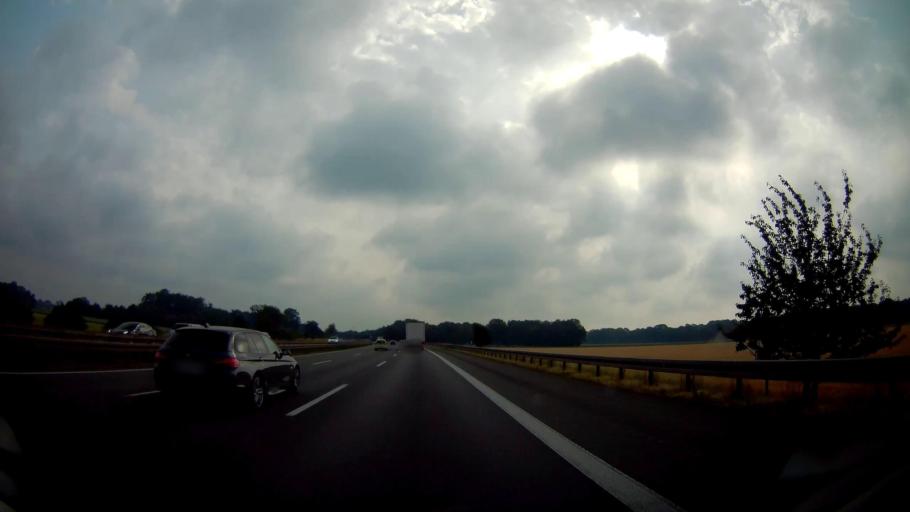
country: DE
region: North Rhine-Westphalia
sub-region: Regierungsbezirk Detmold
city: Guetersloh
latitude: 51.8727
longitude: 8.4109
